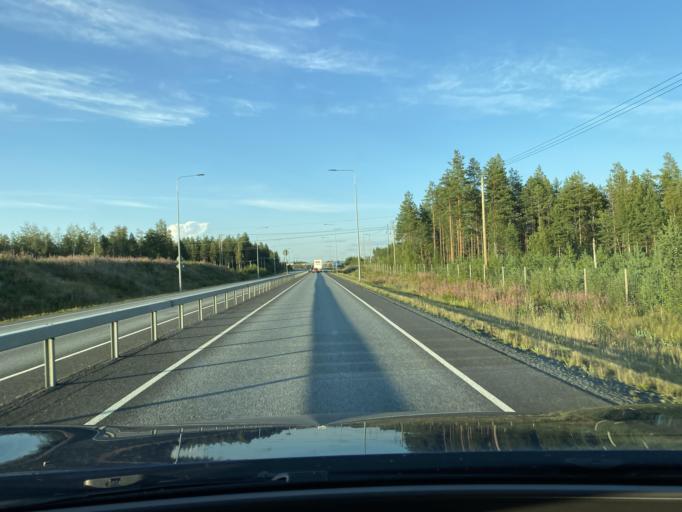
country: FI
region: Southern Ostrobothnia
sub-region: Seinaejoki
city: Seinaejoki
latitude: 62.7195
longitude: 22.8648
